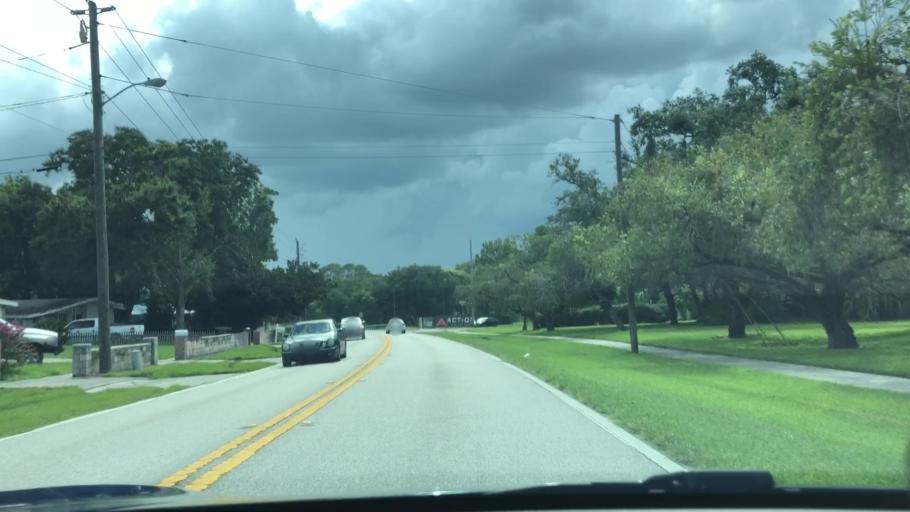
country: US
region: Florida
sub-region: Seminole County
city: Sanford
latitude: 28.7712
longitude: -81.2698
